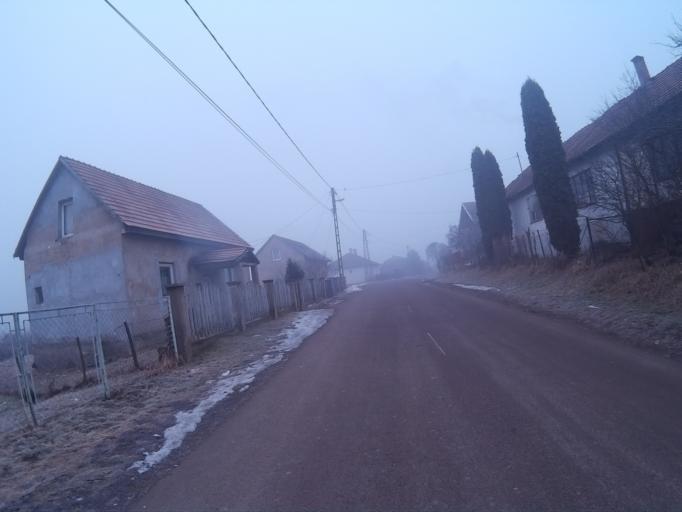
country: HU
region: Nograd
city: Matraverebely
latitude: 47.9766
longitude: 19.7744
